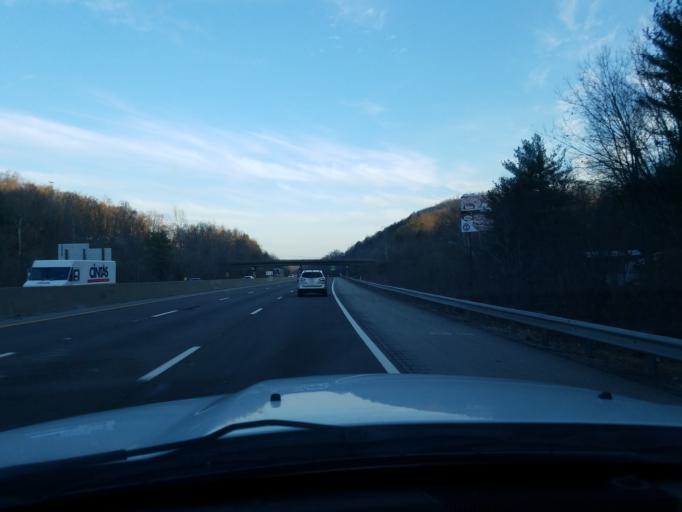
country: US
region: West Virginia
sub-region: Kanawha County
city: Nitro
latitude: 38.4320
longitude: -81.8262
